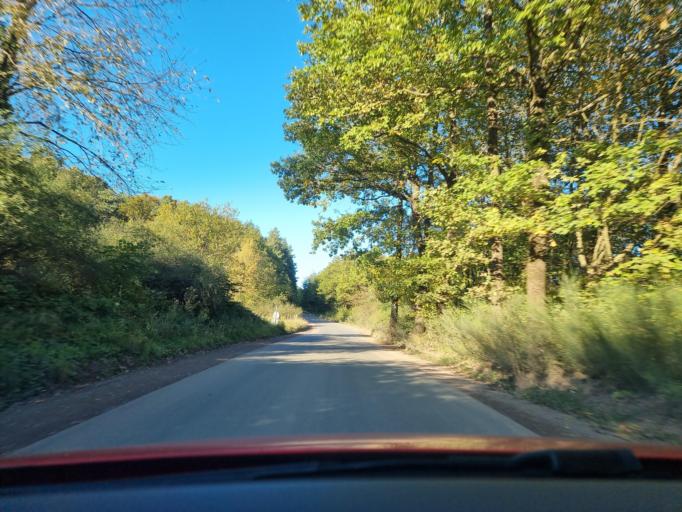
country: DE
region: Rheinland-Pfalz
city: Neumagen-Dhron
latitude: 49.8750
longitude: 6.8864
